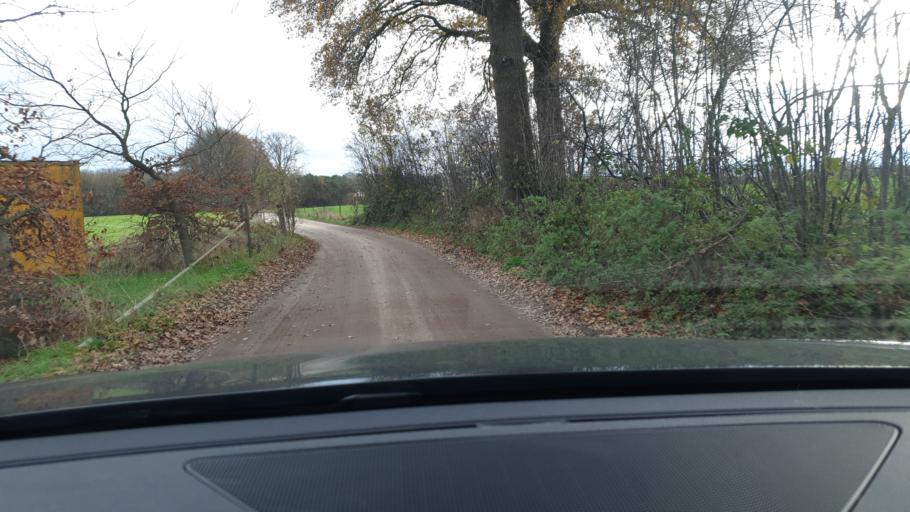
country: NL
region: North Brabant
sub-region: Gemeente Waalre
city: Waalre
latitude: 51.3778
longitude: 5.4342
